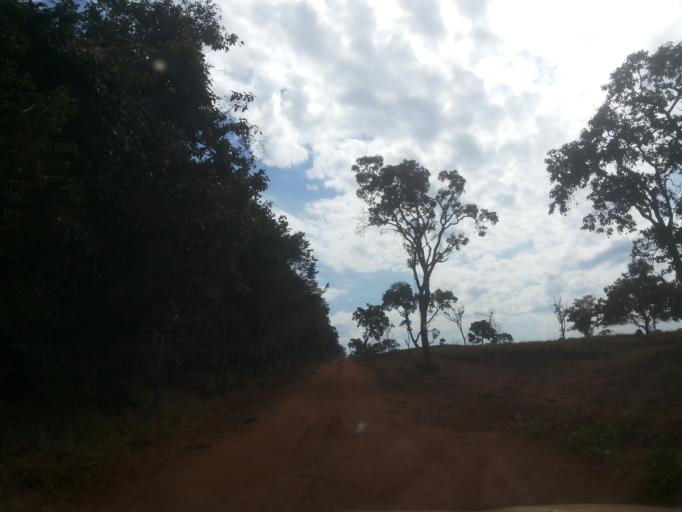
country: BR
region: Minas Gerais
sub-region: Ituiutaba
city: Ituiutaba
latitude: -19.0738
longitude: -49.3637
